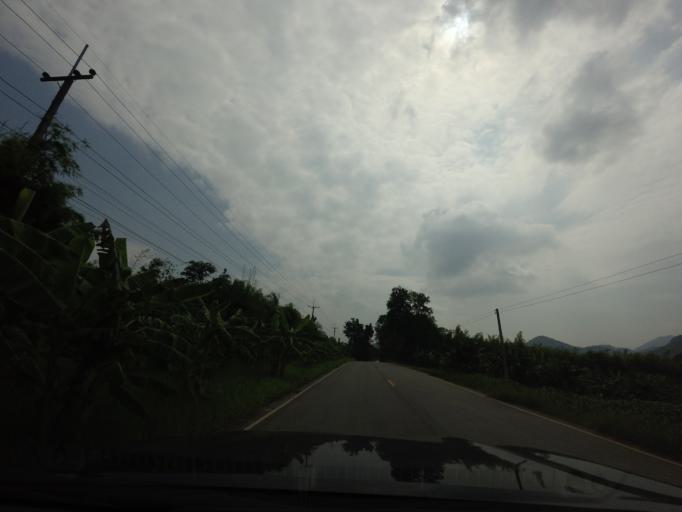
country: TH
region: Loei
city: Tha Li
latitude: 17.6522
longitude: 101.3705
